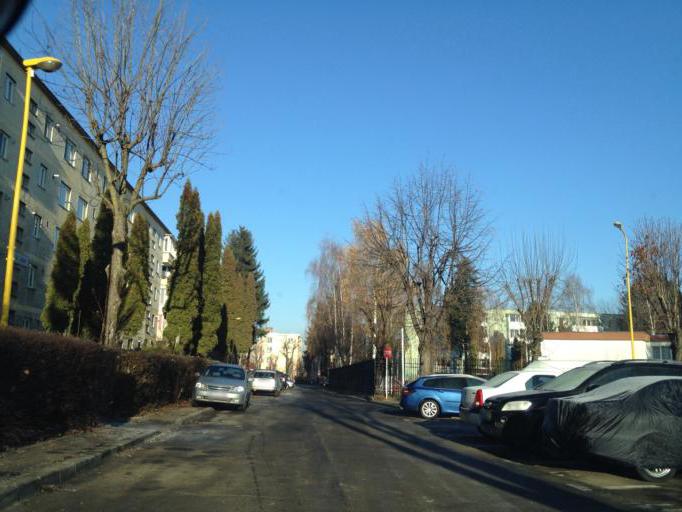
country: RO
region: Brasov
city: Brasov
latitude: 45.6401
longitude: 25.6296
